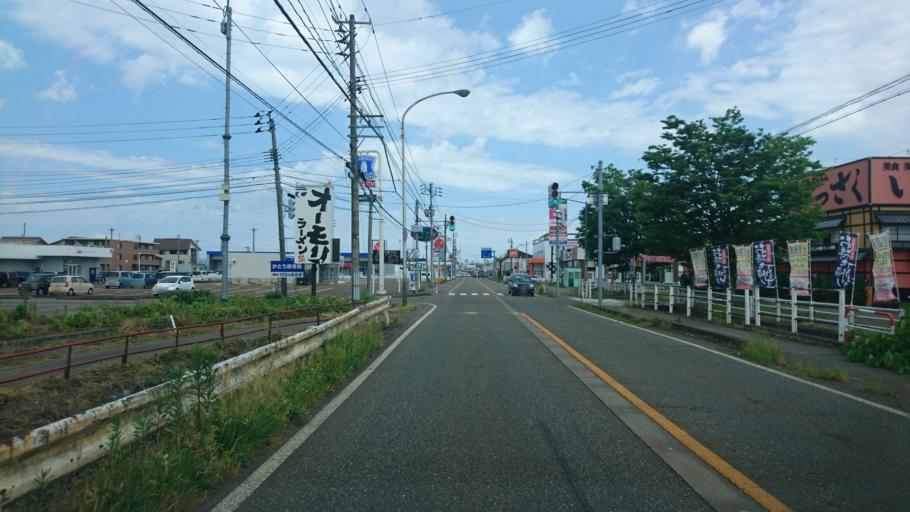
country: JP
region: Niigata
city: Arai
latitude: 37.0535
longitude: 138.2605
